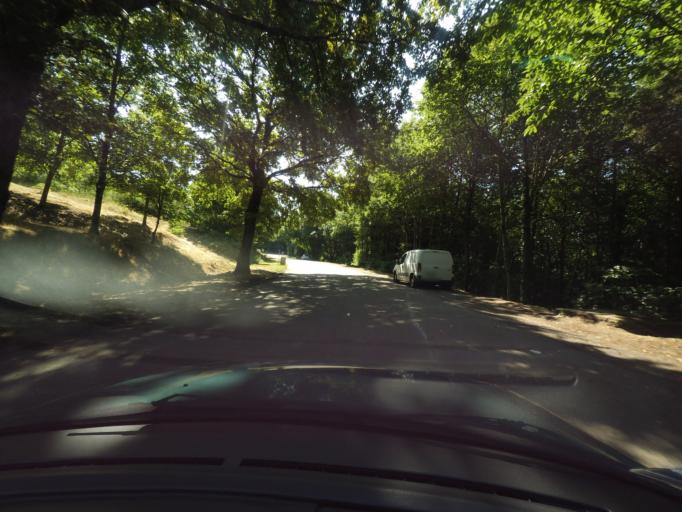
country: FR
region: Limousin
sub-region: Departement de la Haute-Vienne
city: Nieul
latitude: 45.9258
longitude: 1.1967
